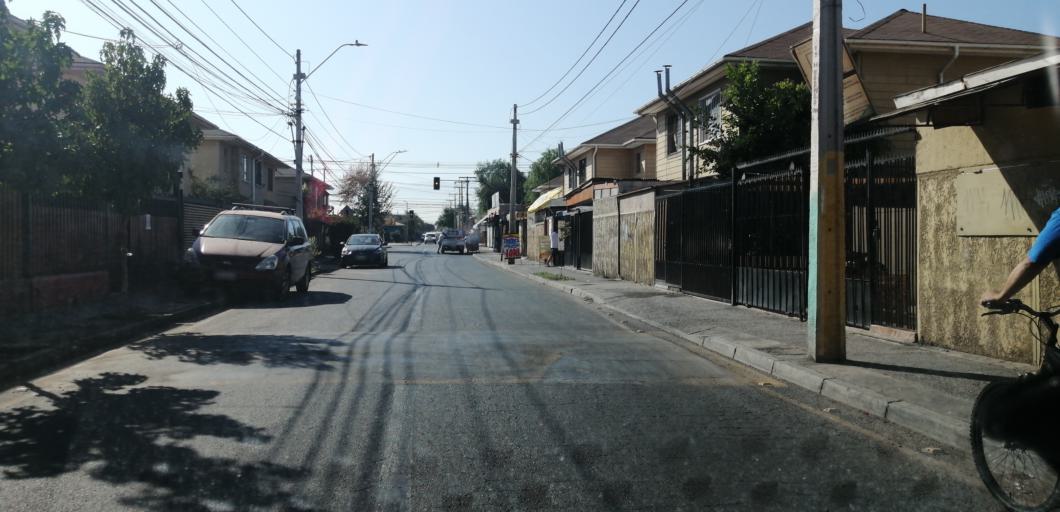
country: CL
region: Santiago Metropolitan
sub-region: Provincia de Santiago
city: Lo Prado
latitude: -33.4347
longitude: -70.7738
